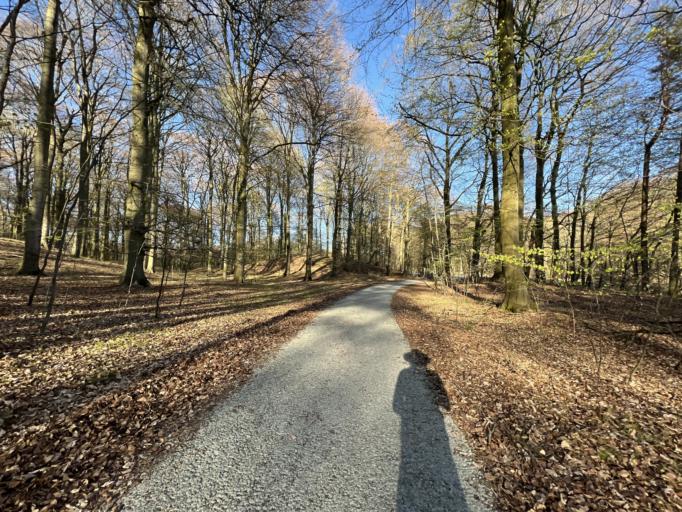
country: DE
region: Mecklenburg-Vorpommern
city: Sassnitz
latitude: 54.5300
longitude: 13.6408
